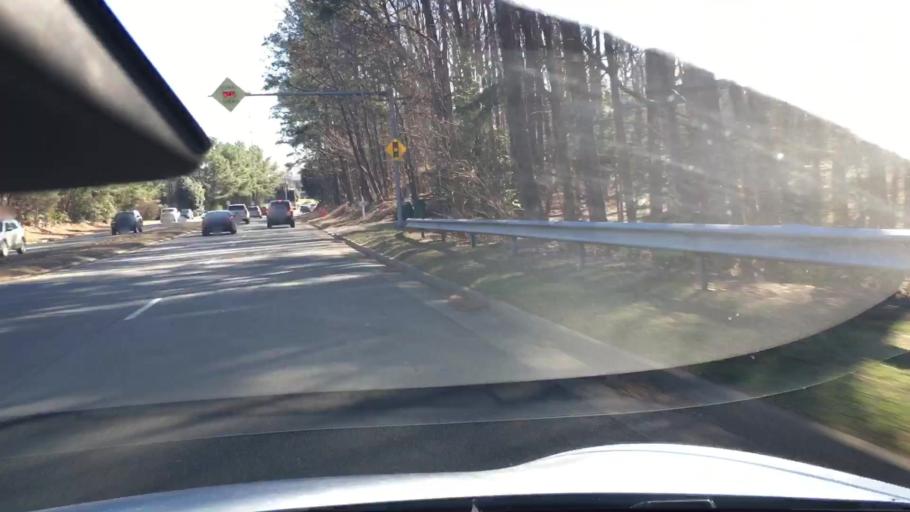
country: US
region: Virginia
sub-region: Henrico County
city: Tuckahoe
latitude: 37.5840
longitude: -77.5700
